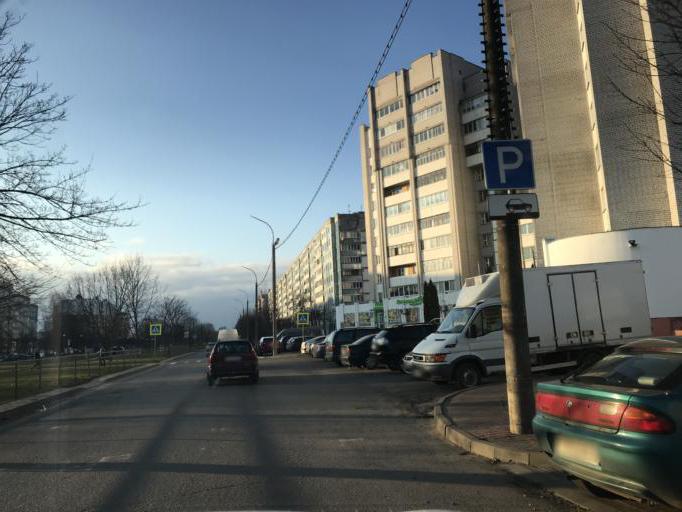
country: BY
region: Mogilev
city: Mahilyow
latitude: 53.8705
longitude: 30.3382
